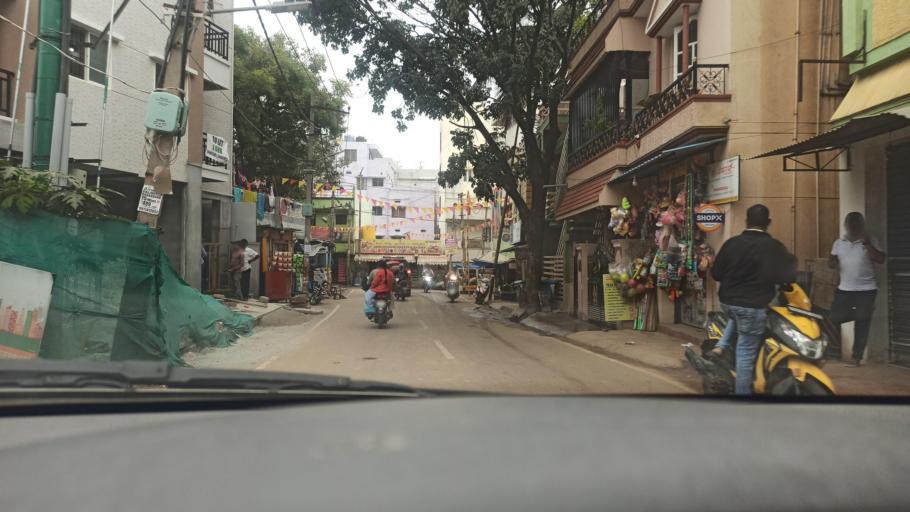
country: IN
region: Karnataka
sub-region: Bangalore Urban
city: Bangalore
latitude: 12.9943
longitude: 77.6793
